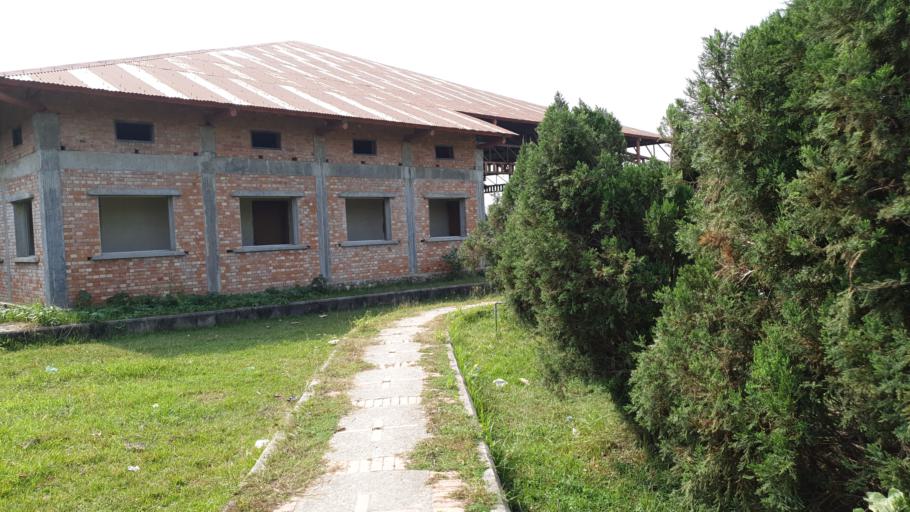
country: NP
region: Central Region
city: Janakpur
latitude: 26.7567
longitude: 85.9179
